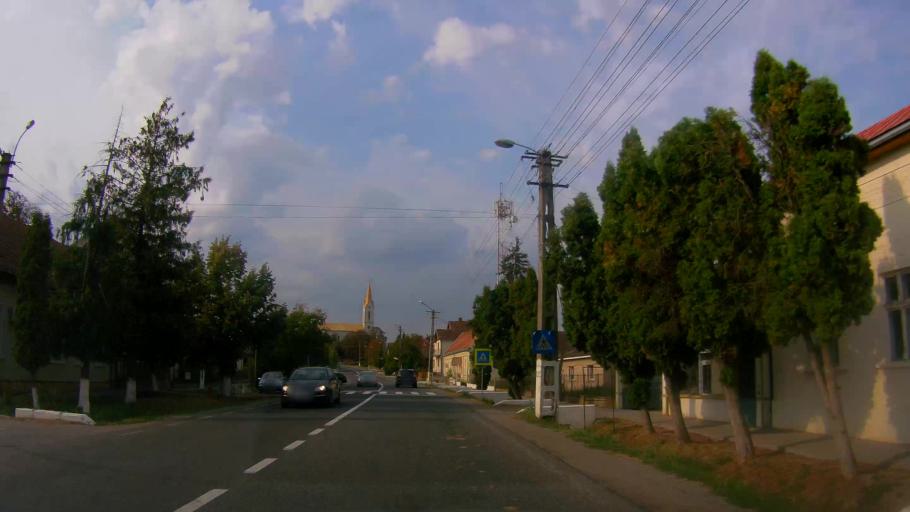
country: RO
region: Satu Mare
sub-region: Oras Ardud
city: Ardud
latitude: 47.6405
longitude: 22.8885
